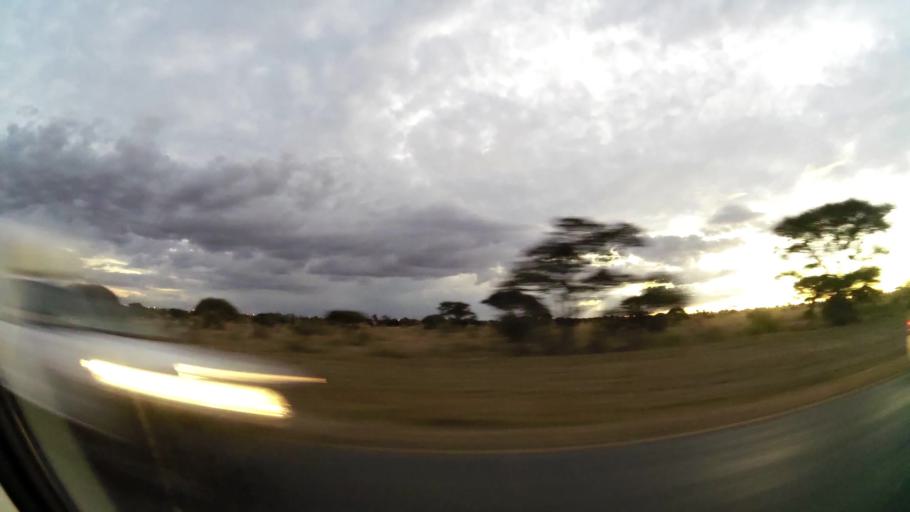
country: ZA
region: Limpopo
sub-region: Capricorn District Municipality
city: Polokwane
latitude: -23.8456
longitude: 29.4279
